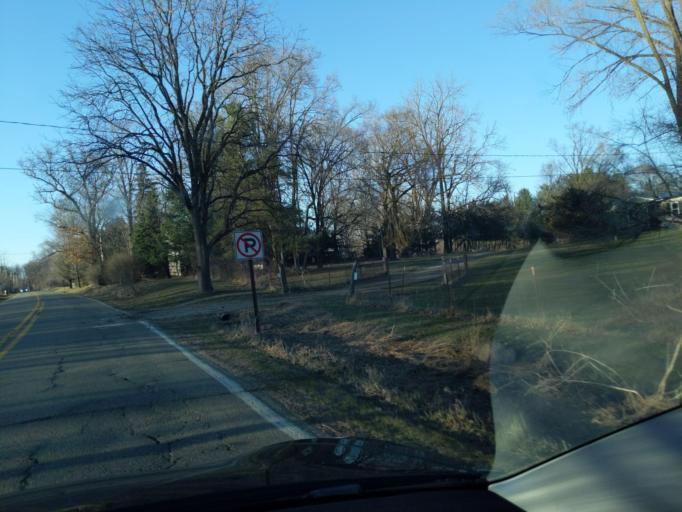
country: US
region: Michigan
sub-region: Livingston County
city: Pinckney
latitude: 42.4350
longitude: -84.0582
